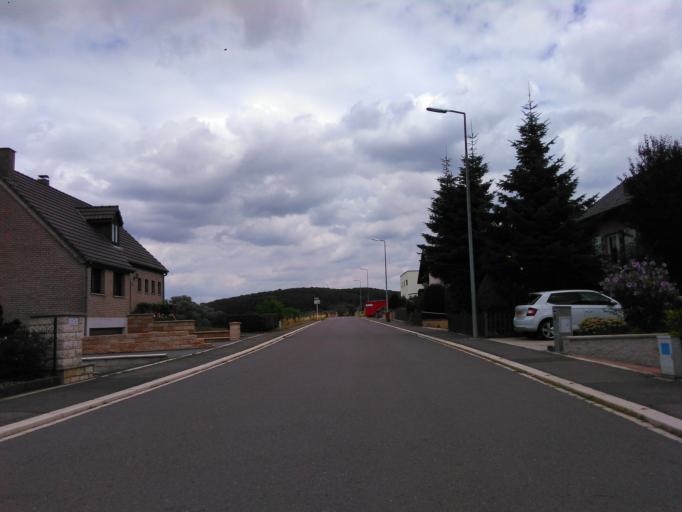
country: LU
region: Grevenmacher
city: Gonderange
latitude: 49.6936
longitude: 6.2551
